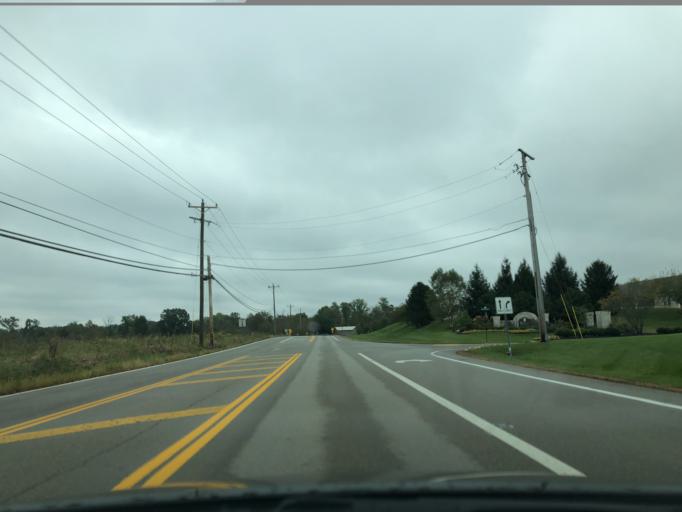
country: US
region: Ohio
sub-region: Hamilton County
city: Loveland
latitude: 39.2582
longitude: -84.2411
